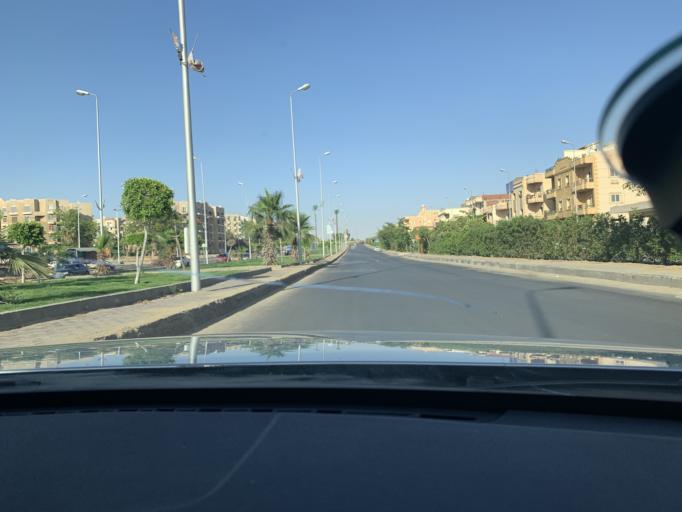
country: EG
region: Muhafazat al Qalyubiyah
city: Al Khankah
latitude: 30.0528
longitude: 31.4567
